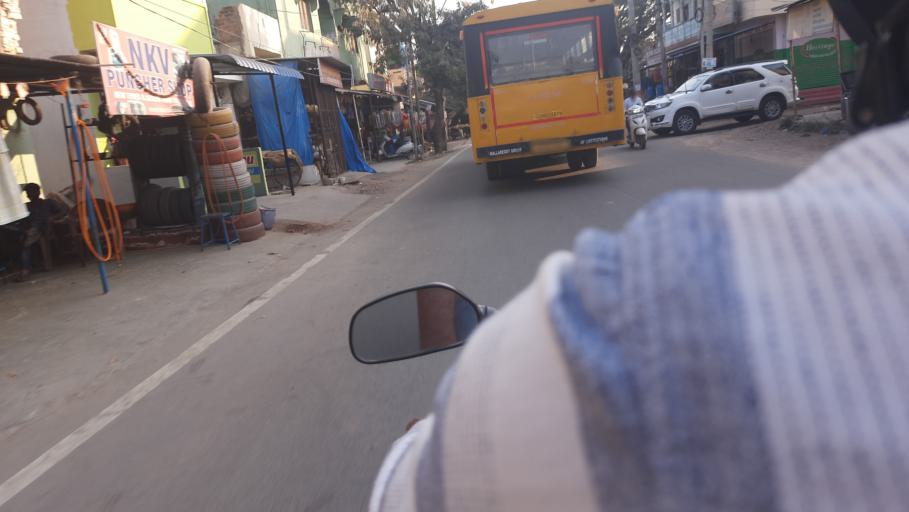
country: IN
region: Telangana
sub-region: Rangareddi
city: Secunderabad
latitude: 17.5062
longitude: 78.5408
